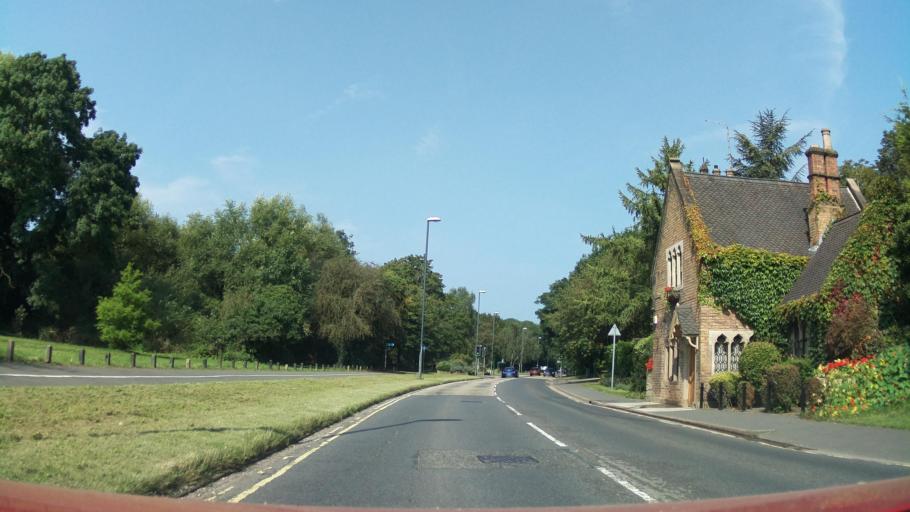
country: GB
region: England
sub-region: Derby
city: Derby
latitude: 52.9373
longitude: -1.5013
